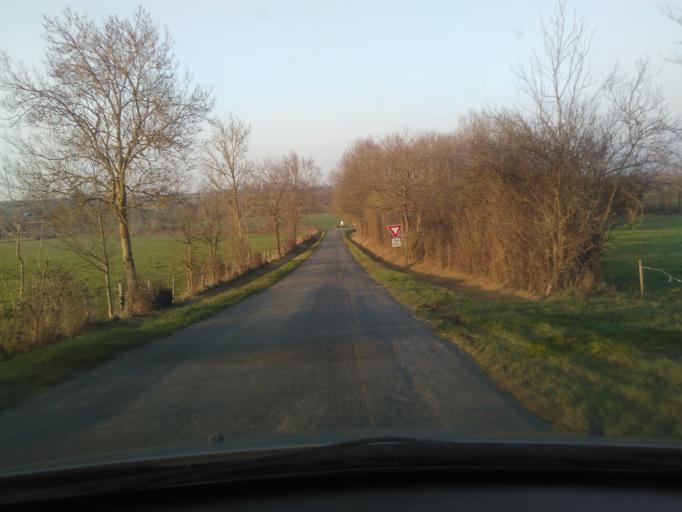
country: FR
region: Pays de la Loire
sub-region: Departement de la Vendee
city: Chantonnay
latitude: 46.6603
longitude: -1.0009
